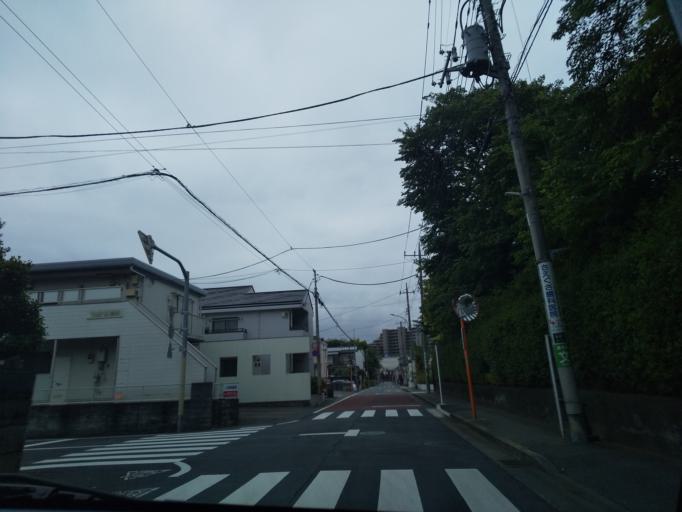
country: JP
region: Tokyo
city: Hino
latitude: 35.6648
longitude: 139.3751
